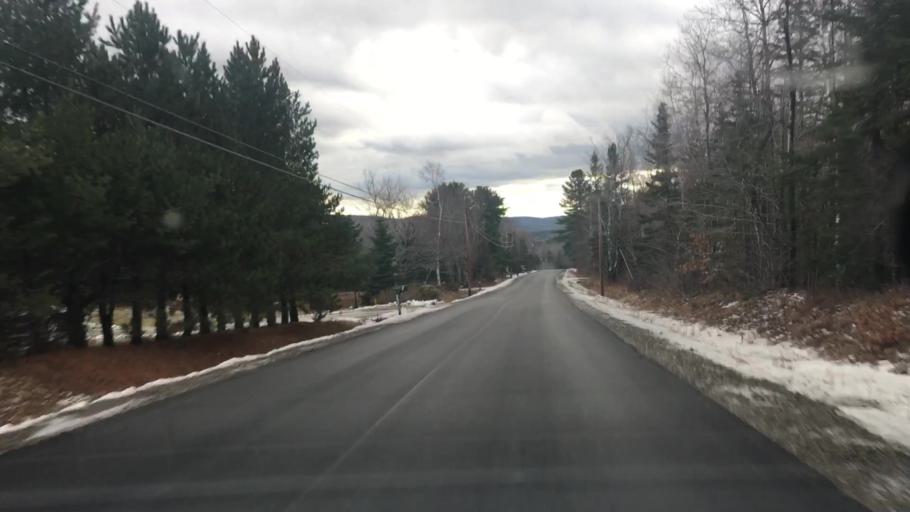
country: US
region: Maine
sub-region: Hancock County
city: Dedham
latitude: 44.6571
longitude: -68.7044
